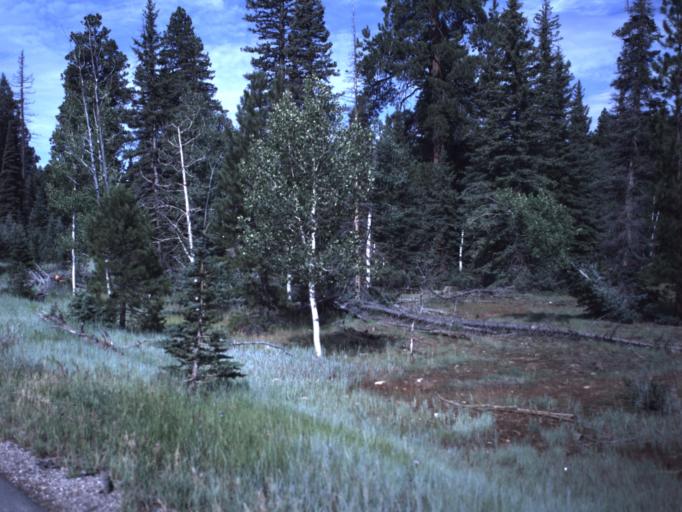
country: US
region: Utah
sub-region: Iron County
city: Parowan
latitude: 37.5188
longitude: -112.6742
